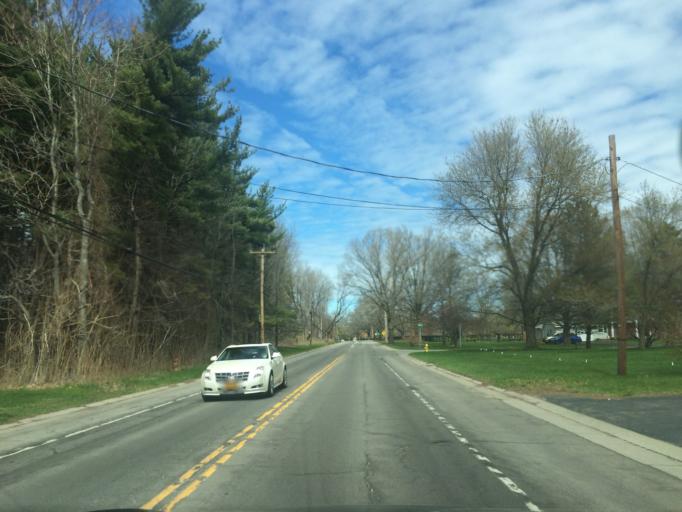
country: US
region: New York
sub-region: Monroe County
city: East Rochester
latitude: 43.0915
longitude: -77.4871
